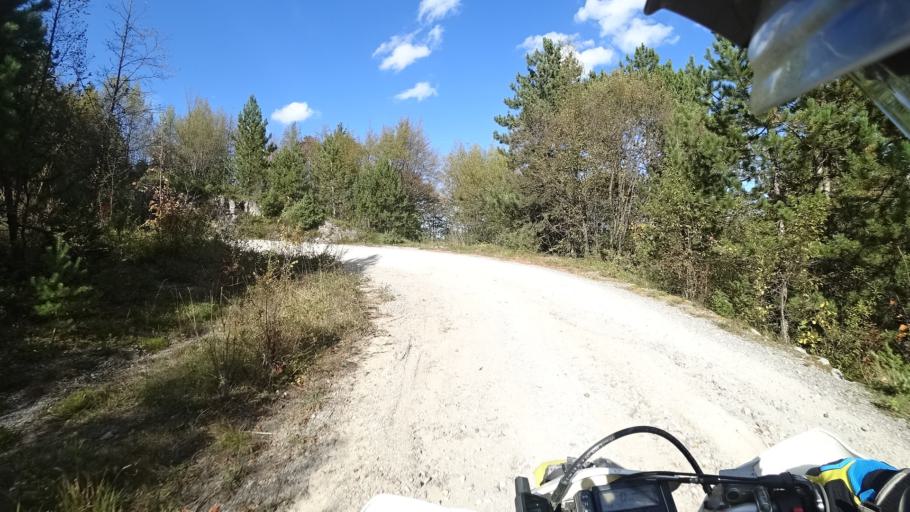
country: HR
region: Karlovacka
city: Plaski
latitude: 45.0708
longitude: 15.3495
